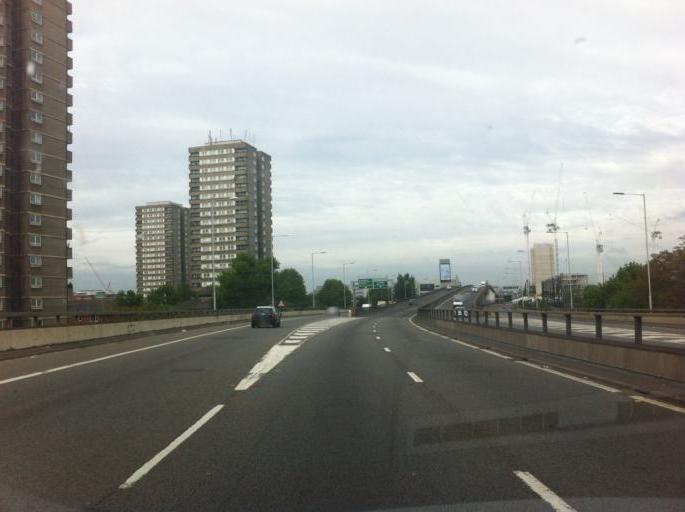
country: GB
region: England
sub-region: Greater London
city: Kensington
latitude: 51.5175
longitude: -0.2109
